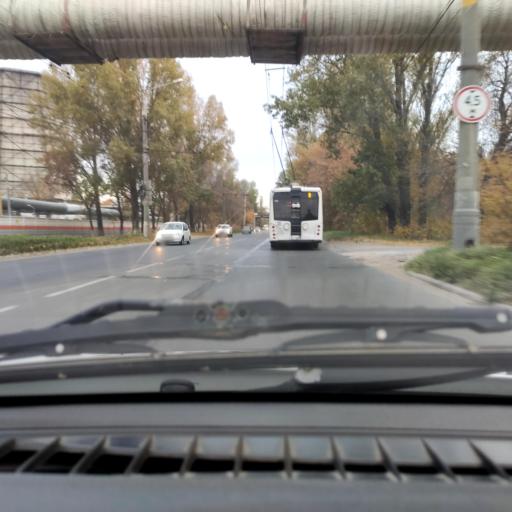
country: RU
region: Samara
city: Tol'yatti
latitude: 53.5509
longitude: 49.4487
